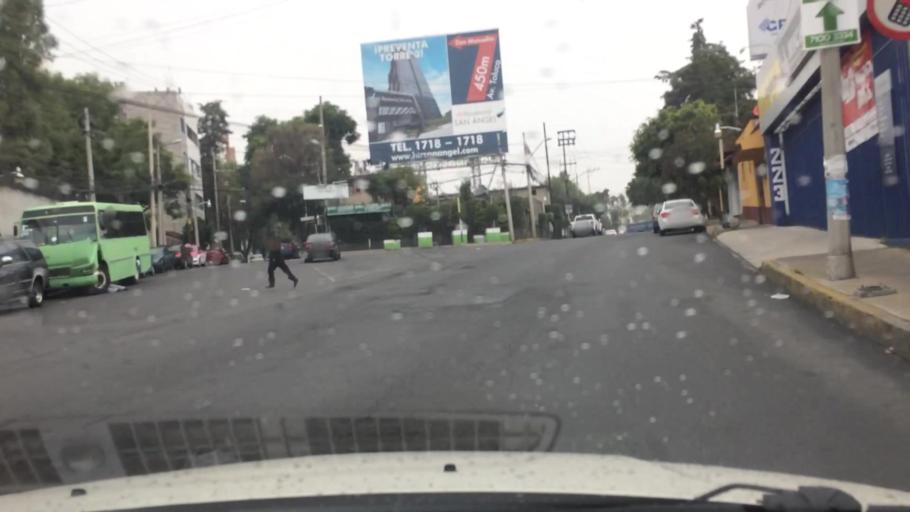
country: MX
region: Mexico City
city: Magdalena Contreras
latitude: 19.3409
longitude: -99.2099
